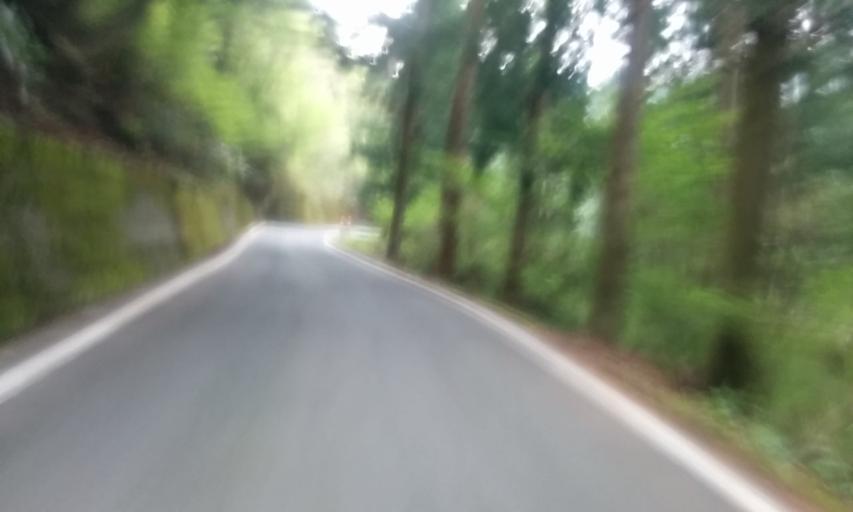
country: JP
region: Ehime
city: Saijo
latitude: 33.8022
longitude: 133.2806
